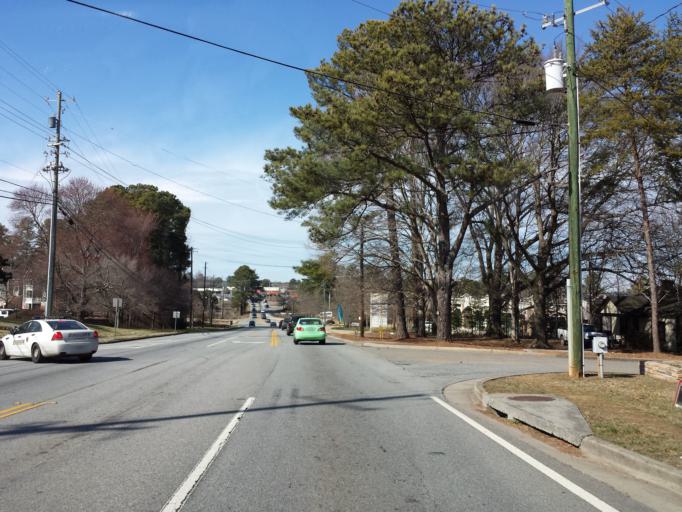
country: US
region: Georgia
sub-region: Cobb County
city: Kennesaw
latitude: 33.9991
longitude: -84.5993
